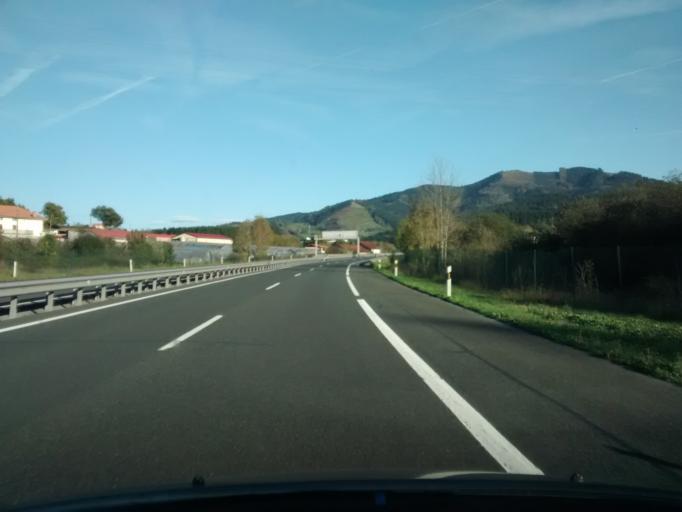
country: ES
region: Basque Country
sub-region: Bizkaia
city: Berriz
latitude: 43.1685
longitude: -2.5682
